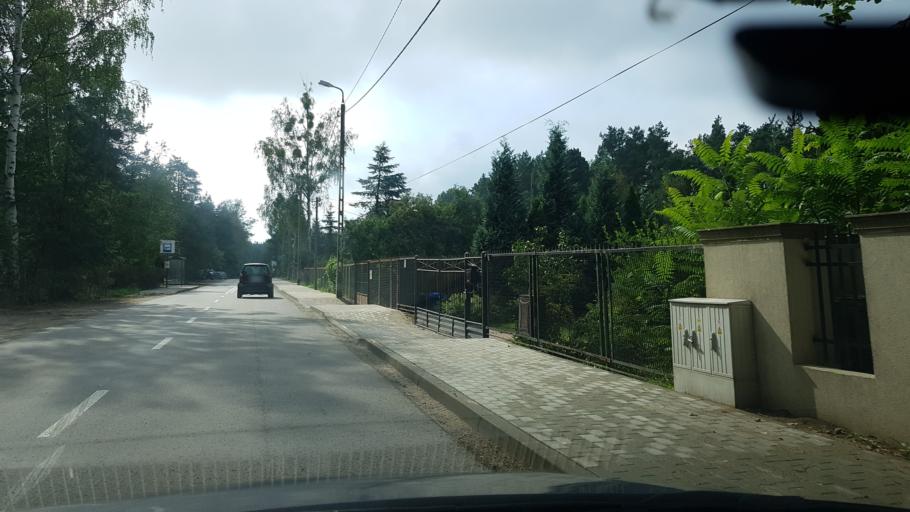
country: PL
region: Masovian Voivodeship
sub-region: Powiat piaseczynski
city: Konstancin-Jeziorna
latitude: 52.0616
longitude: 21.0988
